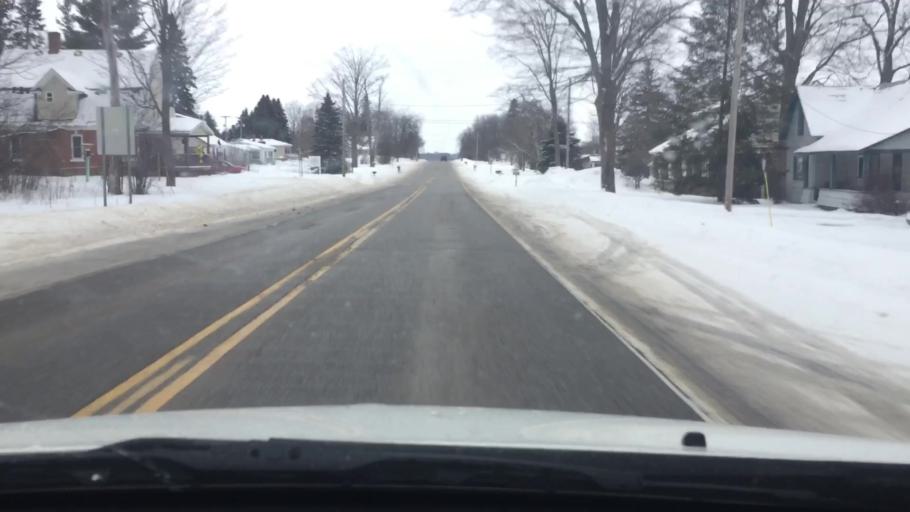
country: US
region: Michigan
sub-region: Charlevoix County
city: East Jordan
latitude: 45.1439
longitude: -85.1398
